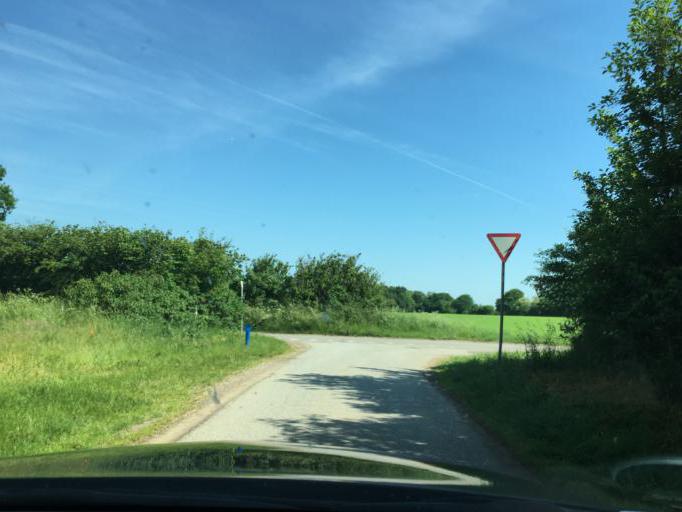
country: DK
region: South Denmark
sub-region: Kolding Kommune
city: Kolding
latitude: 55.5645
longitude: 9.4767
